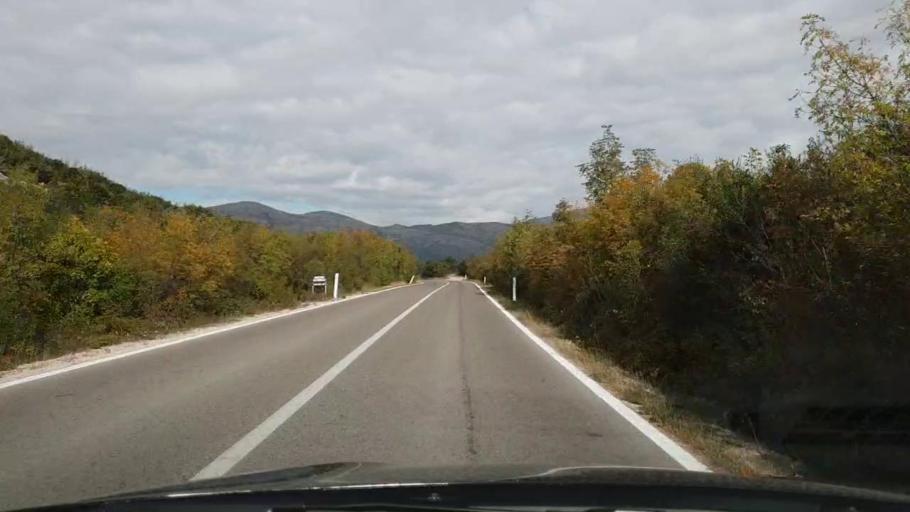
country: HR
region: Dubrovacko-Neretvanska
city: Cibaca
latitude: 42.6836
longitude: 18.2468
